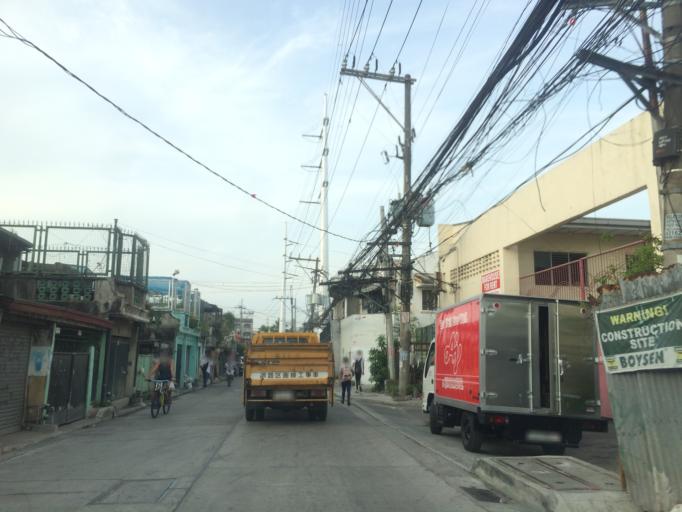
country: PH
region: Calabarzon
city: Del Monte
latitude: 14.6464
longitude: 121.0086
